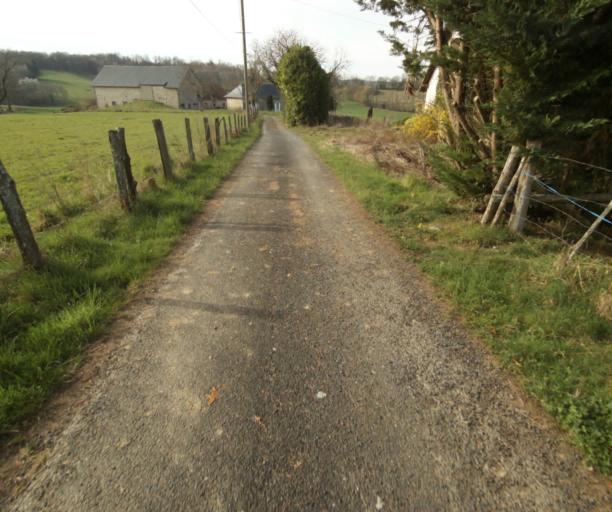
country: FR
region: Limousin
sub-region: Departement de la Correze
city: Chamboulive
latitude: 45.4291
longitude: 1.7411
